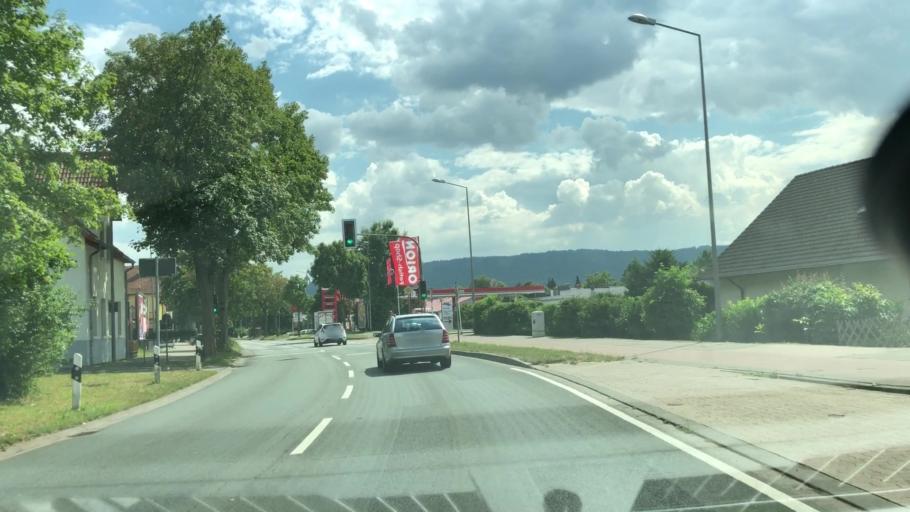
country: DE
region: North Rhine-Westphalia
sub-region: Regierungsbezirk Detmold
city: Minden
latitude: 52.2749
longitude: 8.9017
